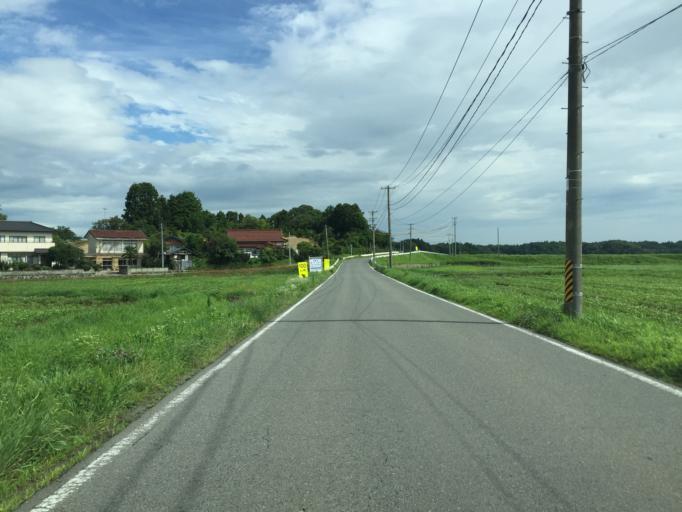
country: JP
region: Miyagi
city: Marumori
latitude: 37.8049
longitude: 140.9562
